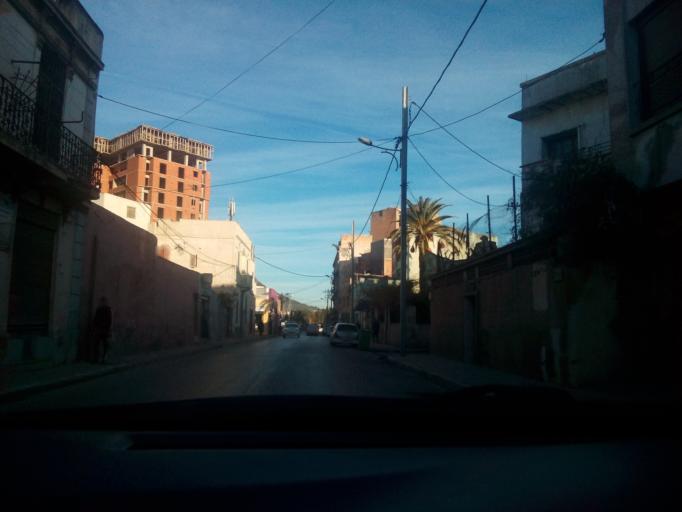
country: DZ
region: Oran
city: Oran
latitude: 35.6903
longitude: -0.6550
